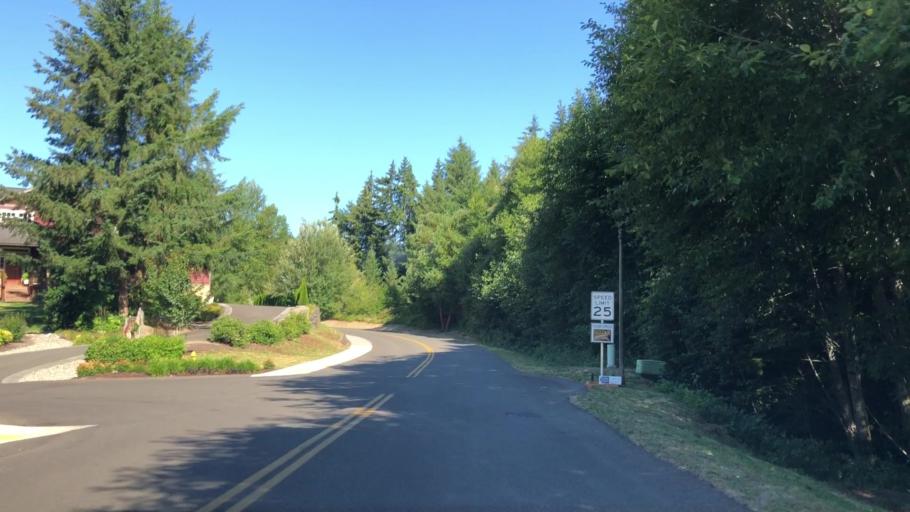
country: US
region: Washington
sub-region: Kitsap County
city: Indianola
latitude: 47.7722
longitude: -122.5203
